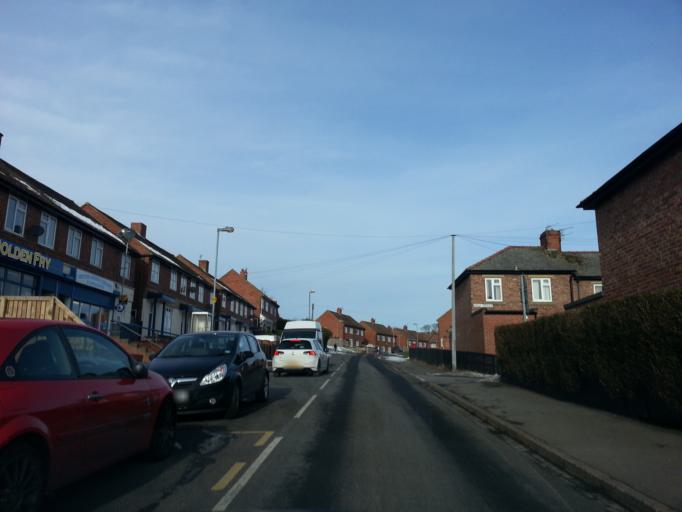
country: GB
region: England
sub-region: County Durham
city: Crook
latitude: 54.7150
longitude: -1.7556
